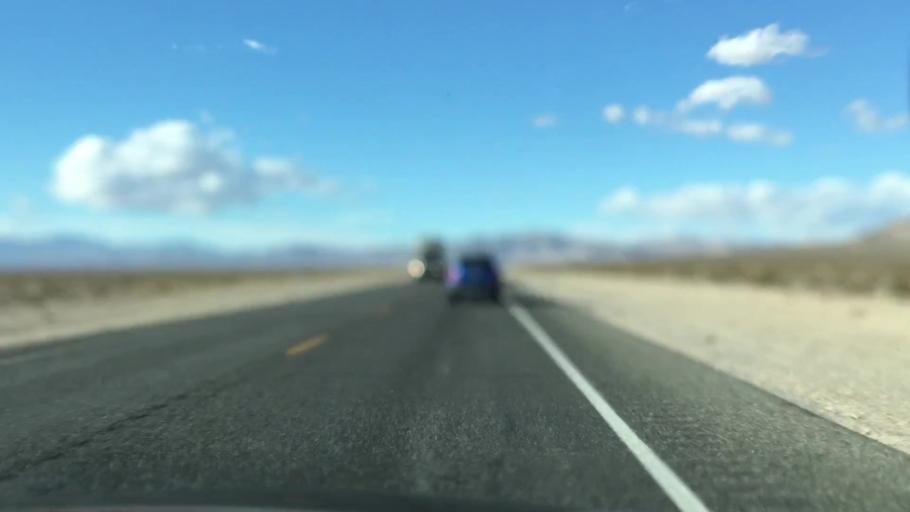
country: US
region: Nevada
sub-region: Nye County
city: Beatty
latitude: 36.7926
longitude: -116.7076
